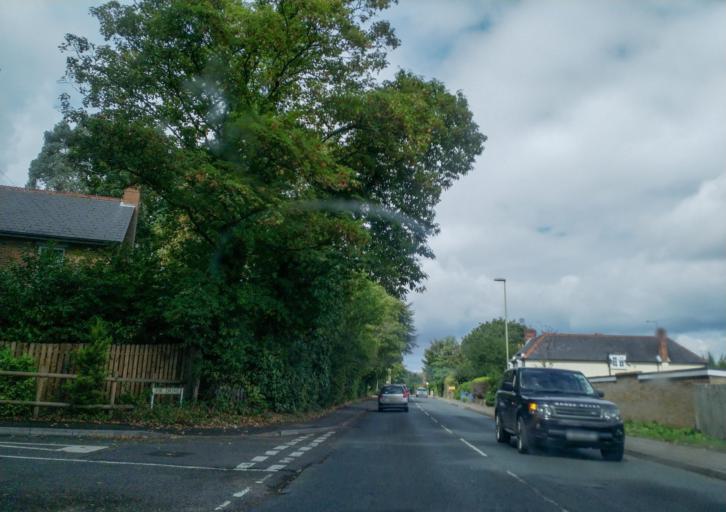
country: GB
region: England
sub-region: Bracknell Forest
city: Sandhurst
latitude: 51.3282
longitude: -0.7825
